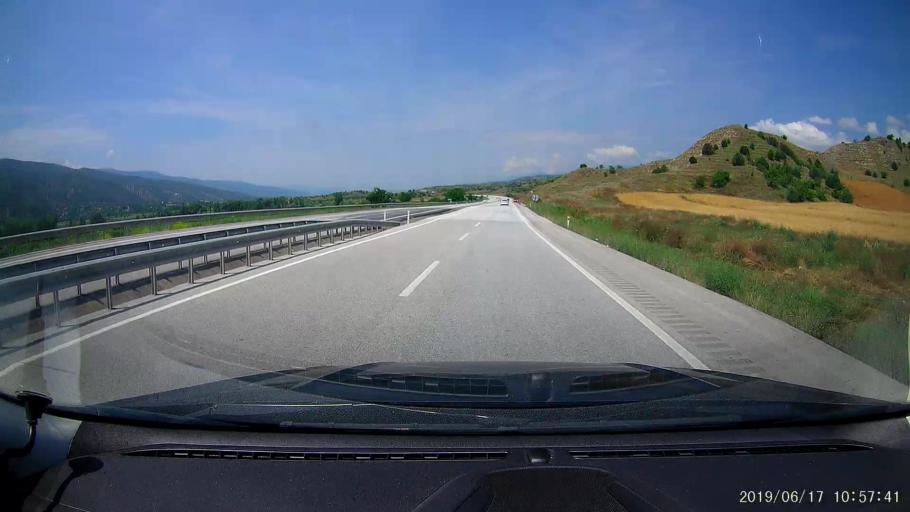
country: TR
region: Kastamonu
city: Tosya
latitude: 41.0482
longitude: 34.2421
